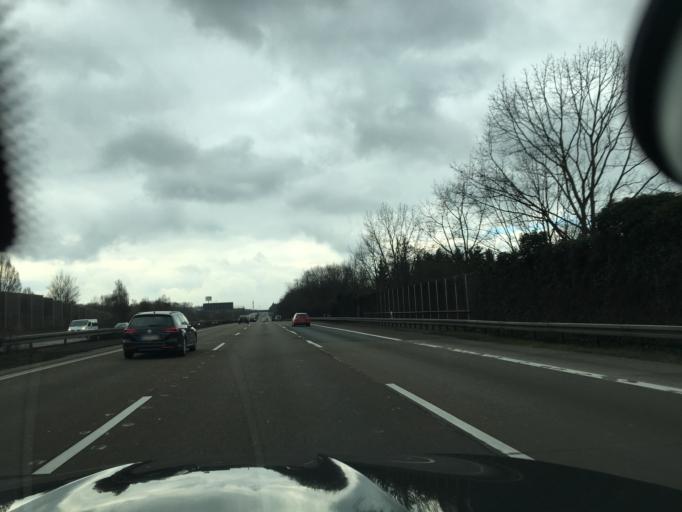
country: DE
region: North Rhine-Westphalia
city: Leichlingen
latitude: 51.1019
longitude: 6.9879
